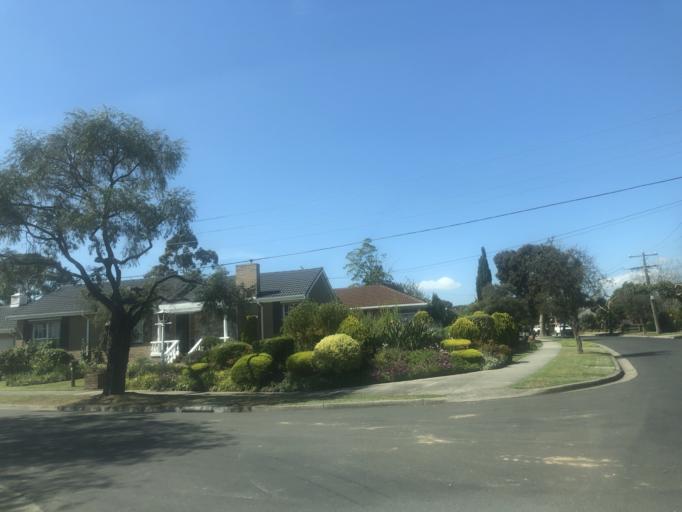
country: AU
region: Victoria
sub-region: Monash
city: Notting Hill
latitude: -37.9007
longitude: 145.1698
